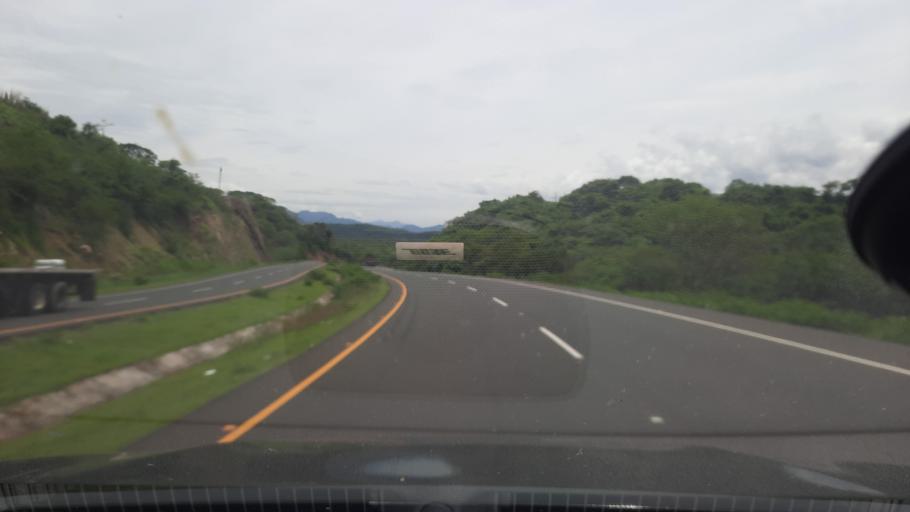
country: HN
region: Valle
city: Aramecina
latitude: 13.6937
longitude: -87.7155
